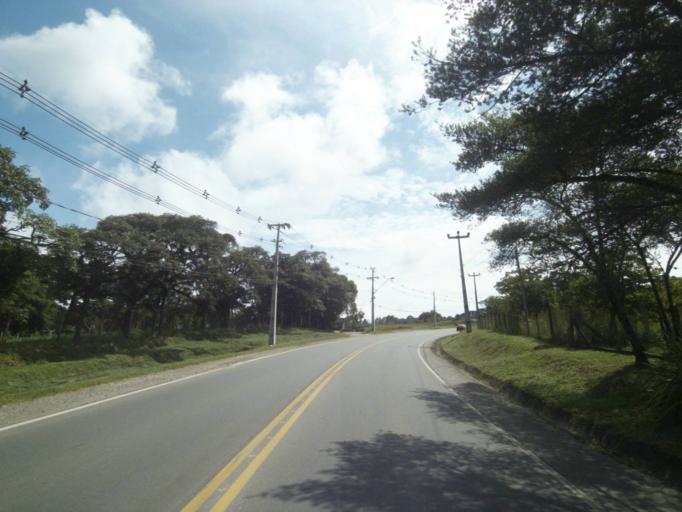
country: BR
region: Parana
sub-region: Campina Grande Do Sul
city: Campina Grande do Sul
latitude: -25.3143
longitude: -49.0731
